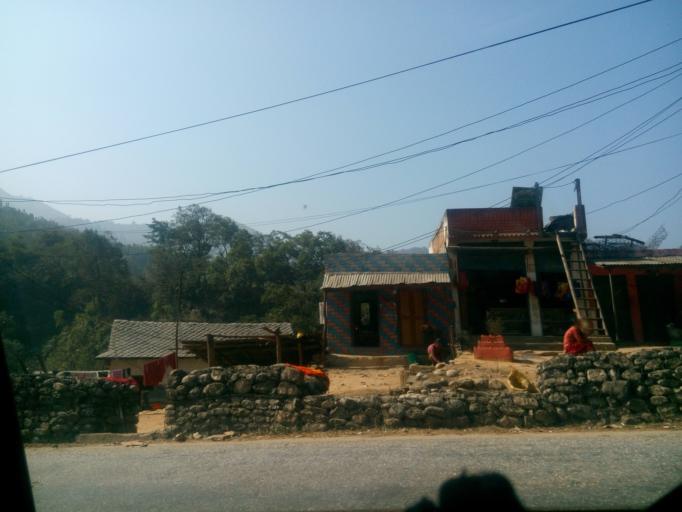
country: NP
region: Central Region
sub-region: Narayani Zone
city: Hitura
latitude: 27.8024
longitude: 84.8722
